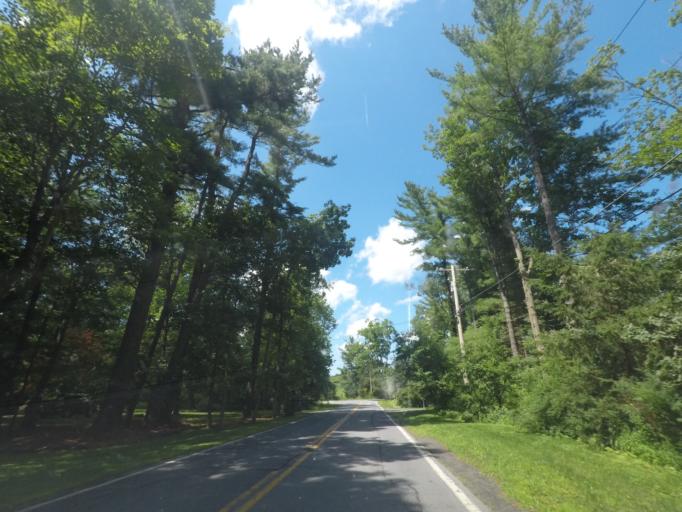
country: US
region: New York
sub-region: Albany County
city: Voorheesville
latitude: 42.6956
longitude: -73.9141
